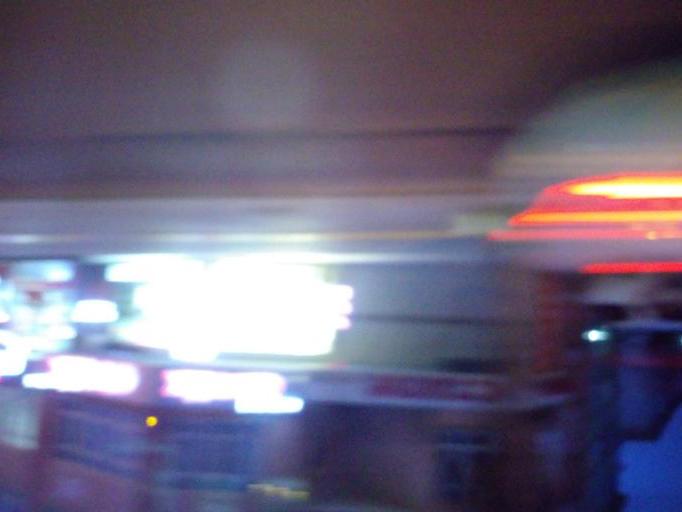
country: TR
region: Ankara
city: Ankara
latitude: 39.9688
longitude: 32.8406
